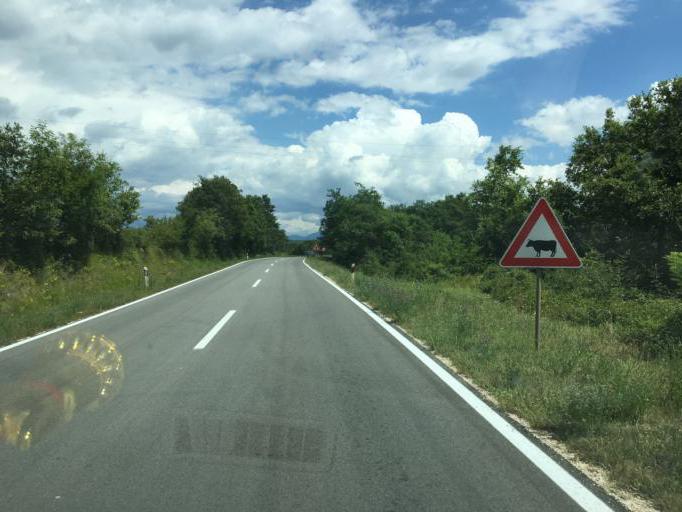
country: HR
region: Istarska
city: Karojba
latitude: 45.2132
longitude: 13.8186
